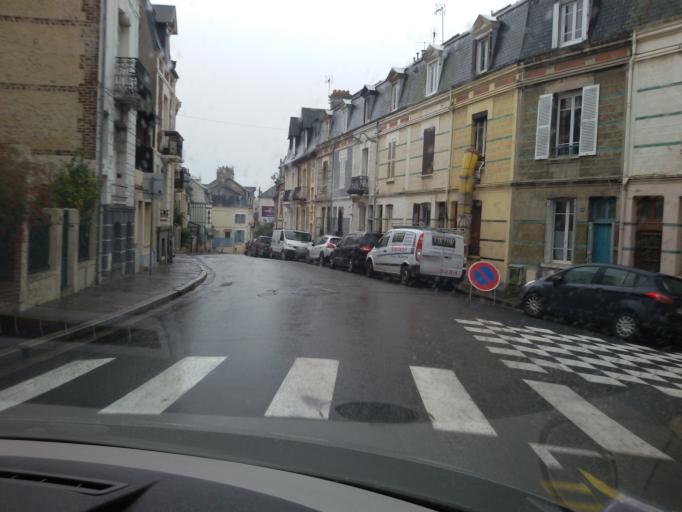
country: FR
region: Lower Normandy
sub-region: Departement du Calvados
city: Trouville-sur-Mer
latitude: 49.3632
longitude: 0.0855
